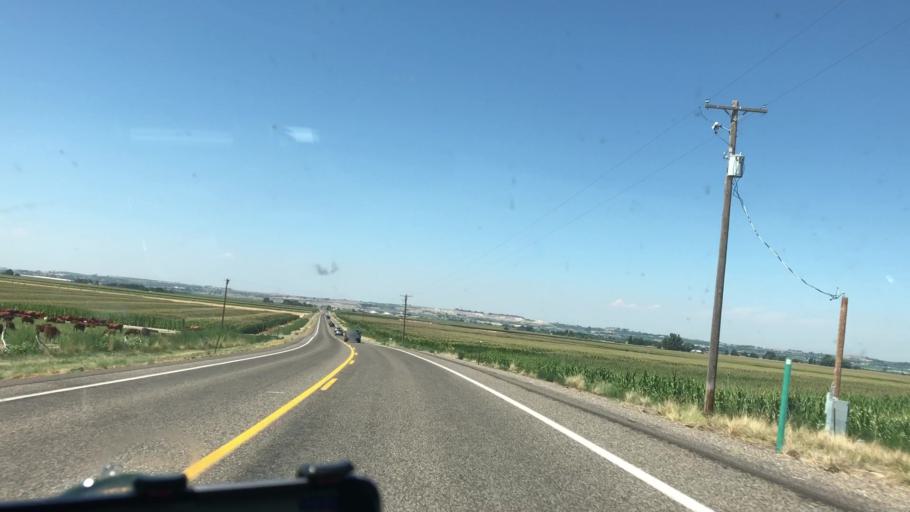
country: US
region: Idaho
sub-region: Owyhee County
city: Marsing
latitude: 43.5223
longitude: -116.8515
